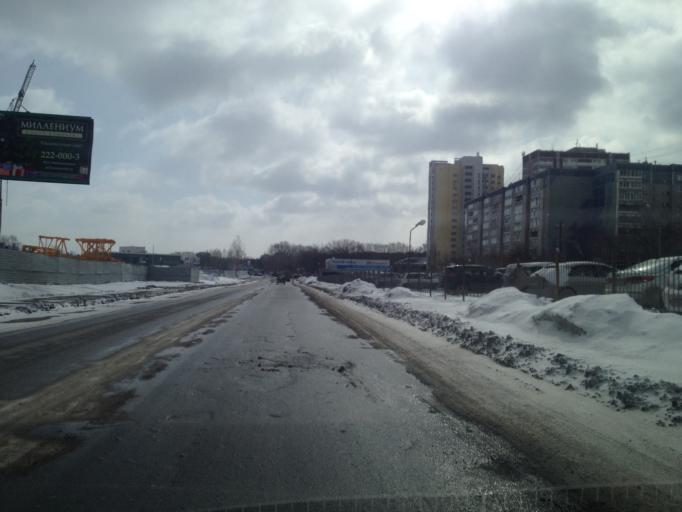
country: RU
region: Sverdlovsk
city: Sovkhoznyy
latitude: 56.8000
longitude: 60.5905
